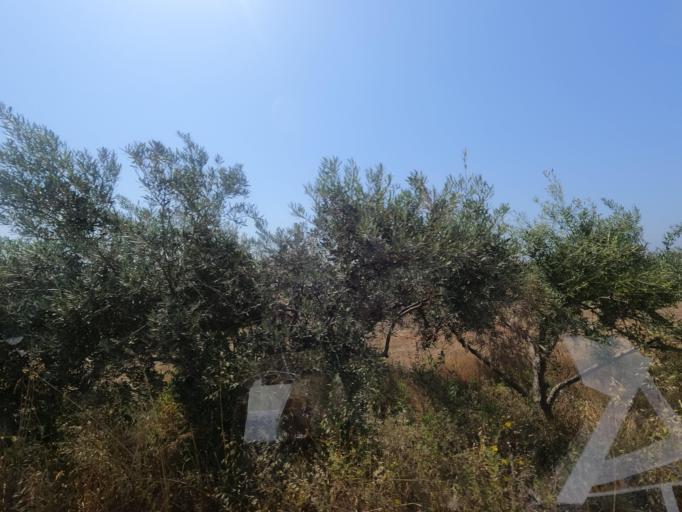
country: CY
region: Ammochostos
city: Avgorou
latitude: 35.0111
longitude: 33.8057
